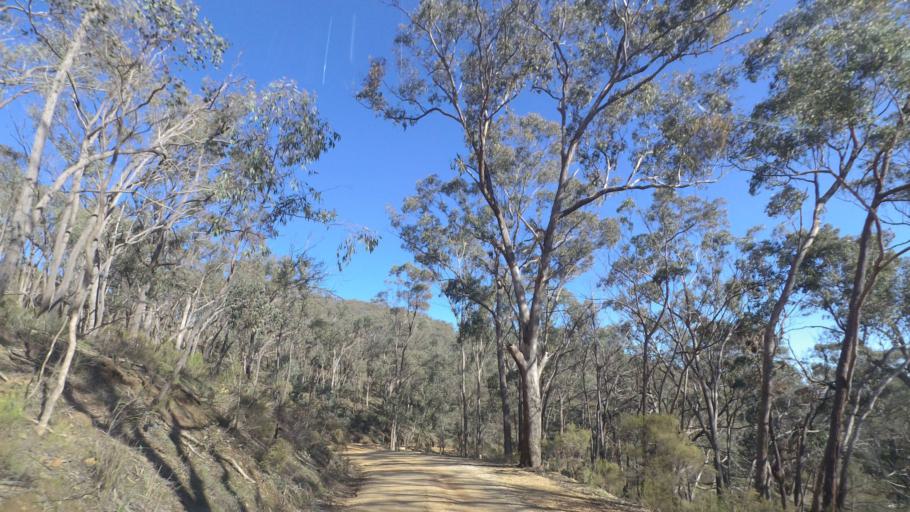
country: AU
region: Victoria
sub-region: Mount Alexander
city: Castlemaine
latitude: -37.0330
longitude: 144.2713
